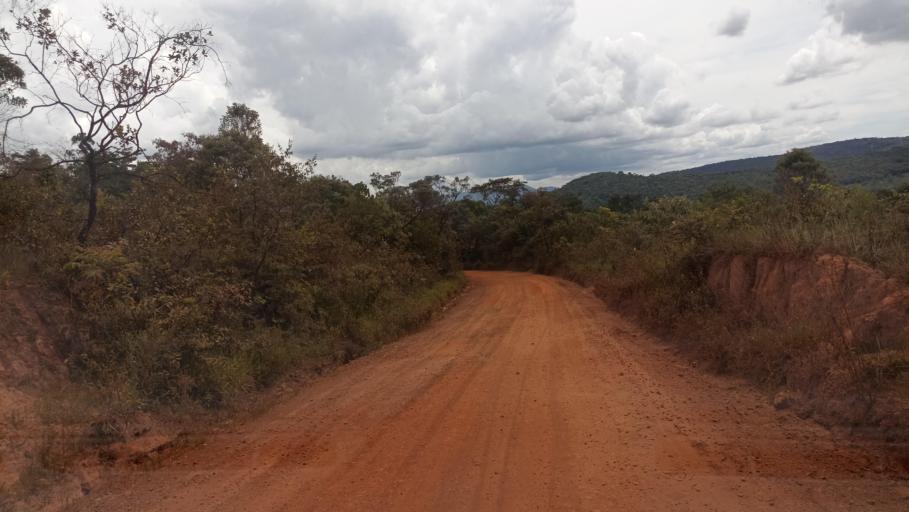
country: BR
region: Minas Gerais
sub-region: Itabirito
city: Itabirito
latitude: -20.3410
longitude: -43.7531
